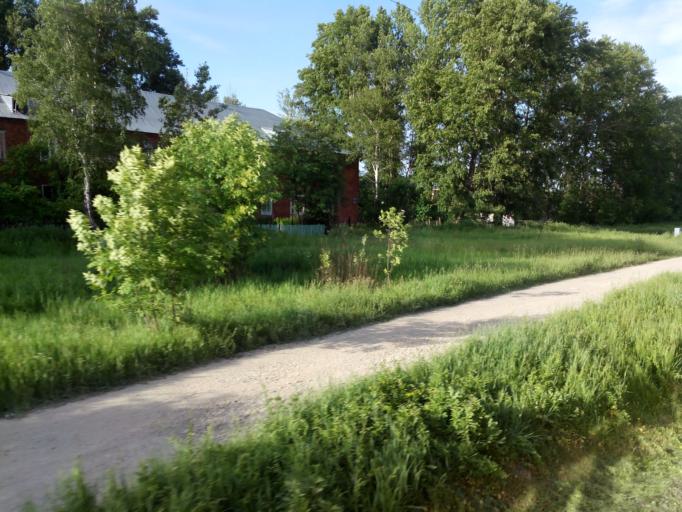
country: RU
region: Moskovskaya
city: Bol'shiye Vyazemy
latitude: 55.6136
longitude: 36.9683
